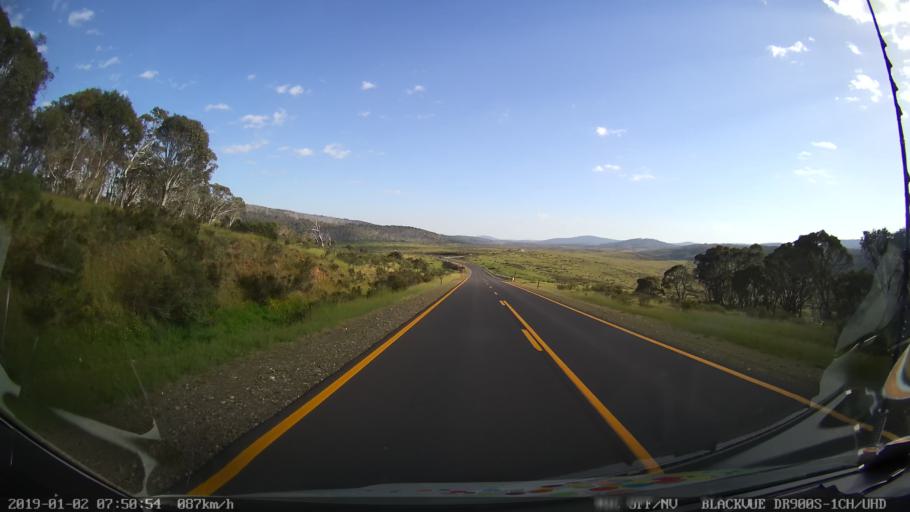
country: AU
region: New South Wales
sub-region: Tumut Shire
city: Tumut
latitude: -35.7249
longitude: 148.5297
